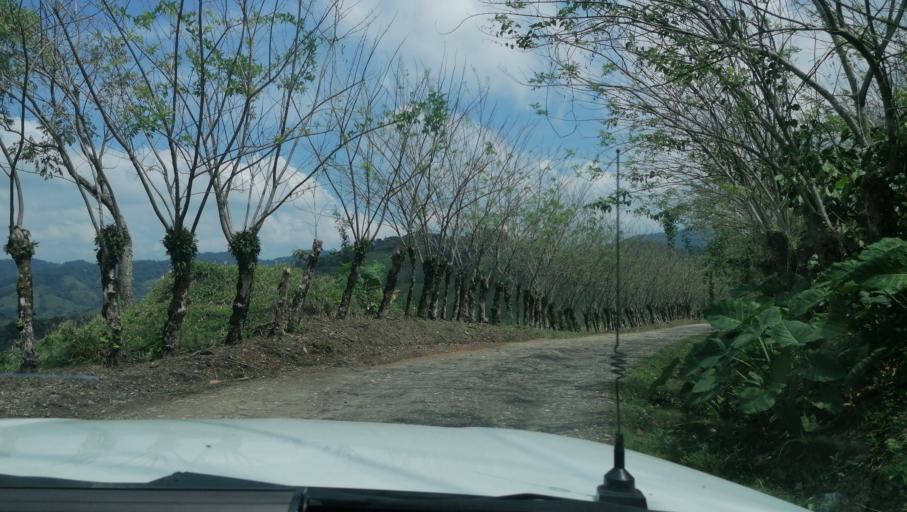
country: MX
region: Chiapas
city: Ixtacomitan
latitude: 17.4392
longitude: -93.2045
